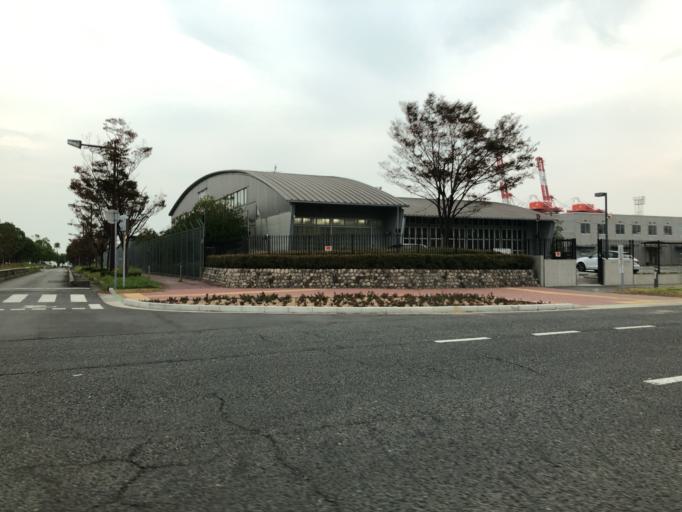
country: JP
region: Hyogo
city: Ashiya
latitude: 34.6829
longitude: 135.2680
